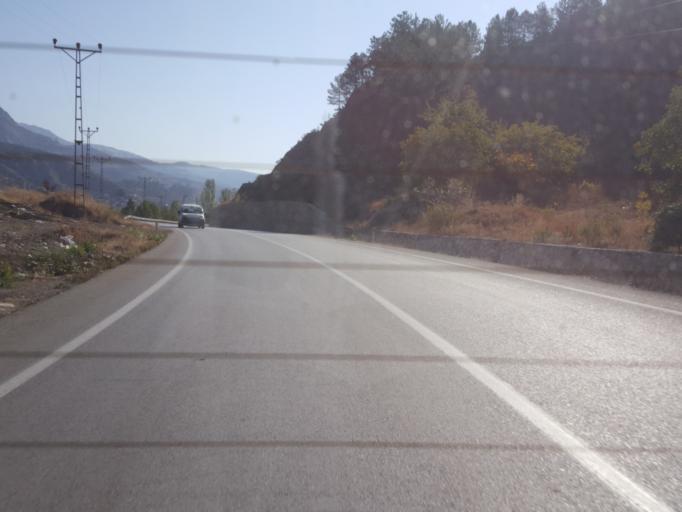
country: TR
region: Corum
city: Iskilip
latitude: 40.7386
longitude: 34.4486
